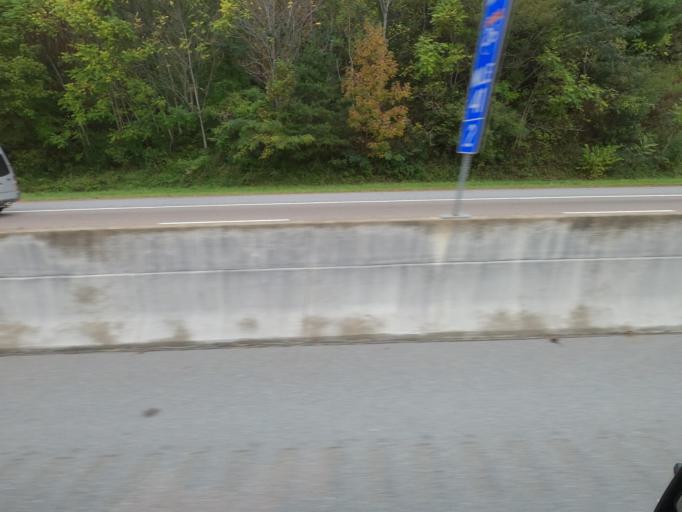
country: US
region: Tennessee
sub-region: Unicoi County
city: Banner Hill
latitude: 36.1072
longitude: -82.4591
